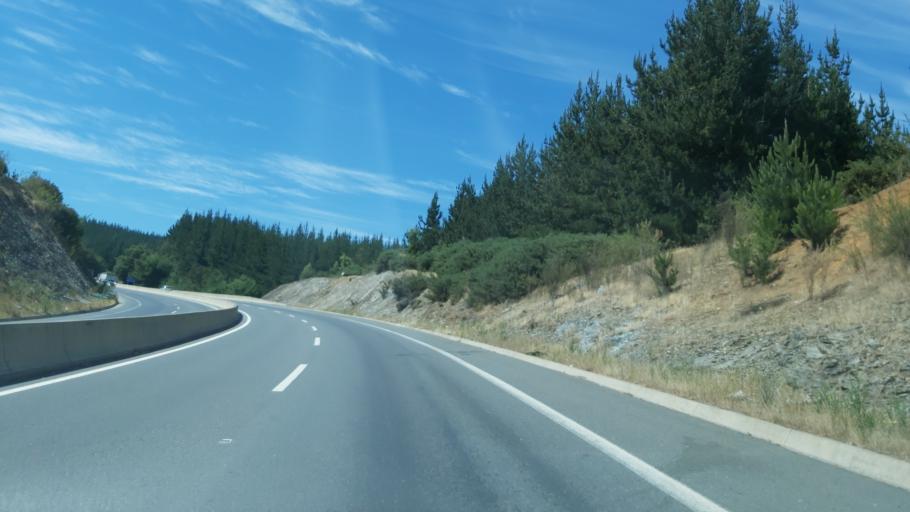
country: CL
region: Biobio
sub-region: Provincia de Concepcion
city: Lota
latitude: -37.0777
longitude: -73.1383
